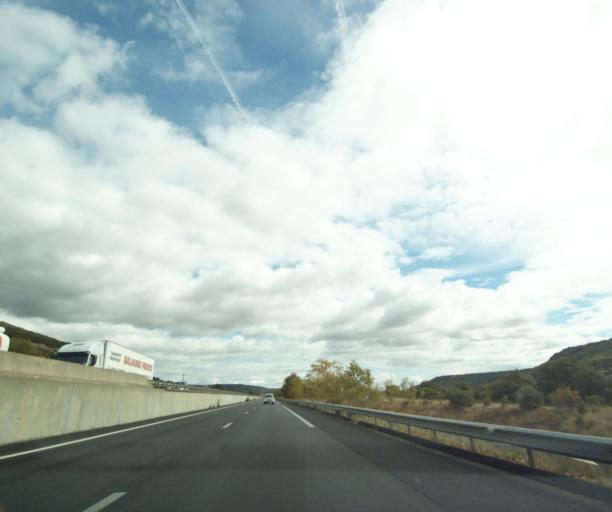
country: FR
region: Languedoc-Roussillon
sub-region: Departement de l'Herault
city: Nebian
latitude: 43.6797
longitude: 3.3952
